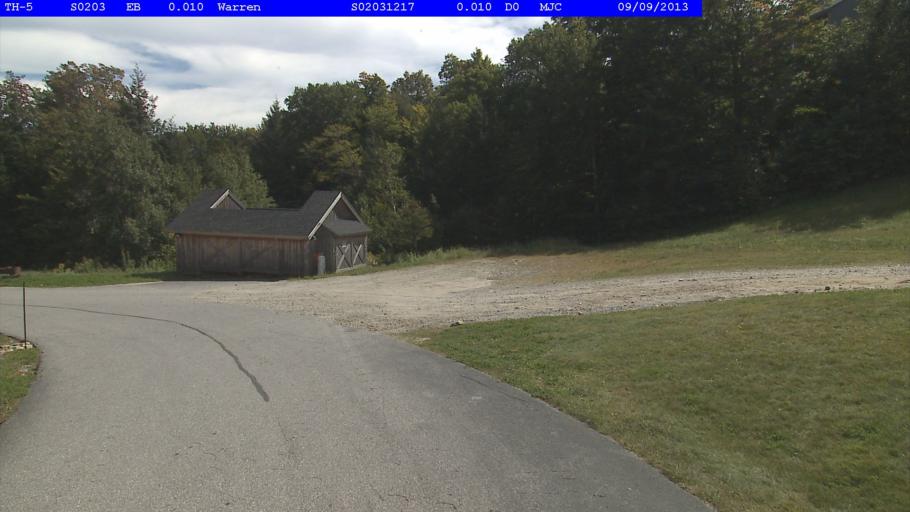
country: US
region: Vermont
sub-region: Addison County
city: Bristol
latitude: 44.1354
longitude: -72.8952
